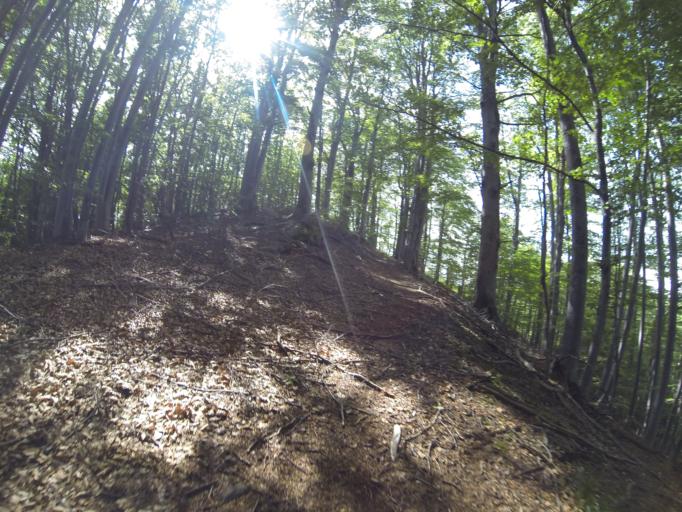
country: RO
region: Valcea
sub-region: Comuna Barbatesti
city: Barbatesti
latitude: 45.2488
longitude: 24.1616
